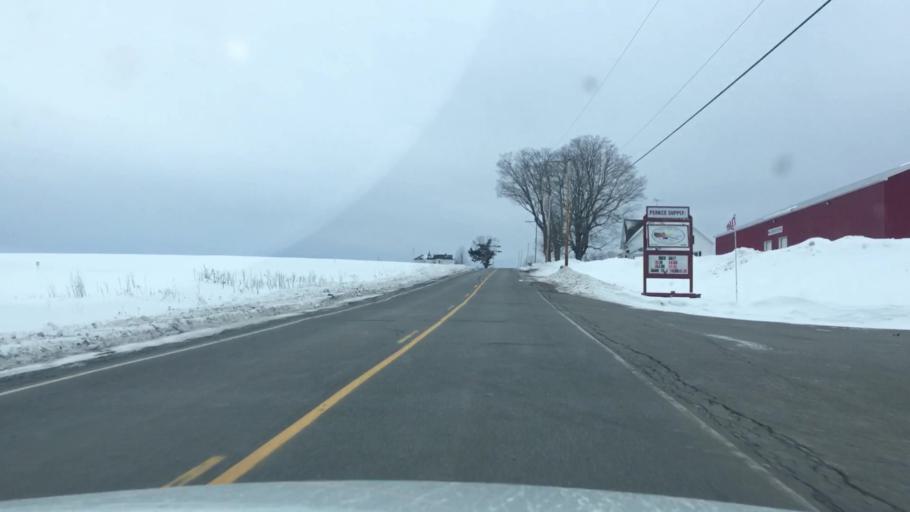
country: US
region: Maine
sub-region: Penobscot County
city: Garland
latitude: 44.9674
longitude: -69.1616
